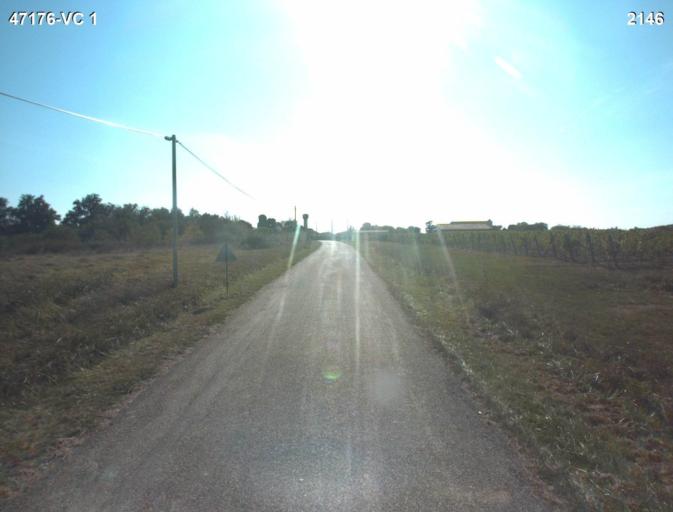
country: FR
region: Aquitaine
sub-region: Departement du Lot-et-Garonne
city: Vianne
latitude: 44.2113
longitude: 0.2965
